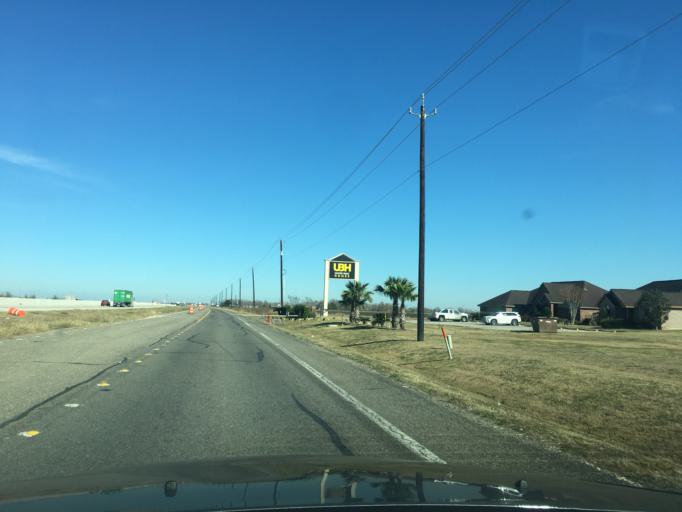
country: US
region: Texas
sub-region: Wharton County
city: East Bernard
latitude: 29.4531
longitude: -95.9869
